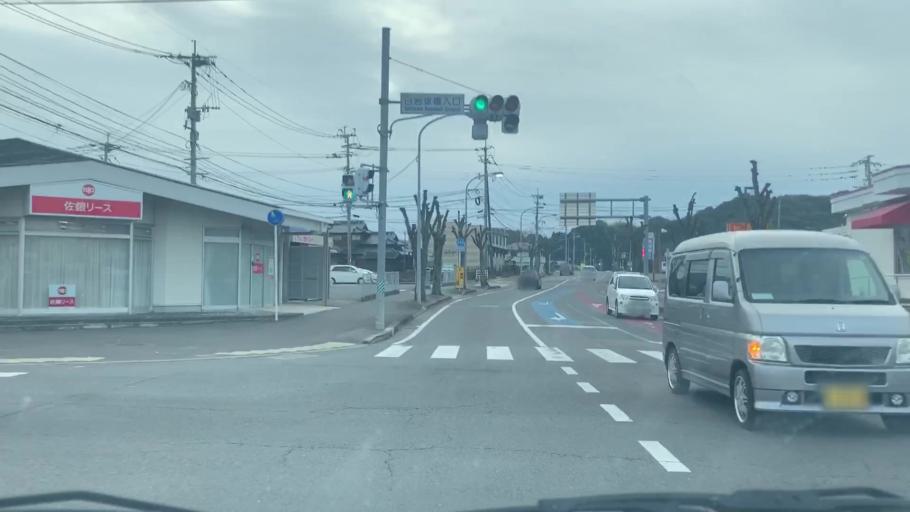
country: JP
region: Saga Prefecture
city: Takeocho-takeo
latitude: 33.1950
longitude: 130.0295
